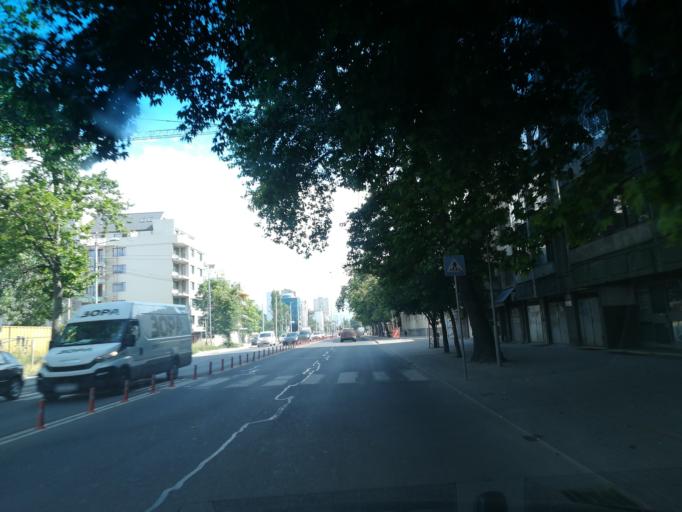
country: BG
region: Plovdiv
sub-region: Obshtina Plovdiv
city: Plovdiv
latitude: 42.1493
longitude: 24.7632
